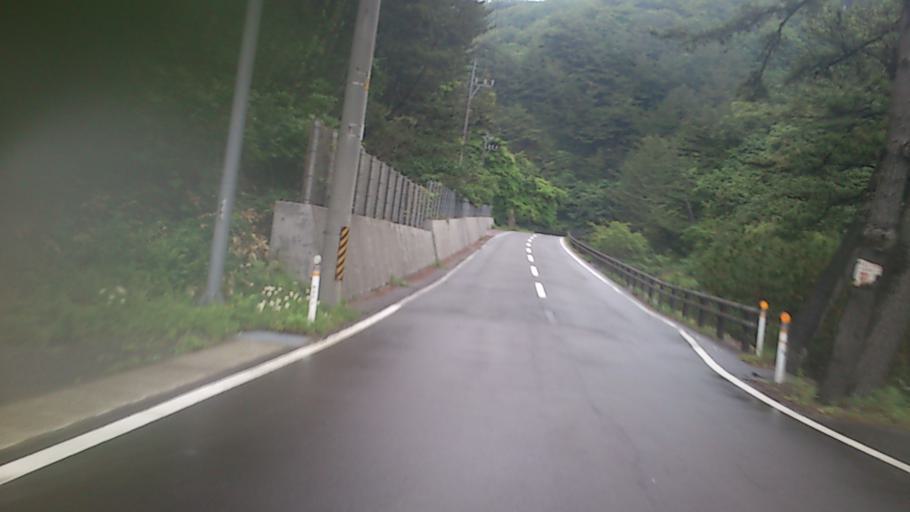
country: JP
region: Akita
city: Noshiromachi
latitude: 40.5508
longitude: 139.9431
